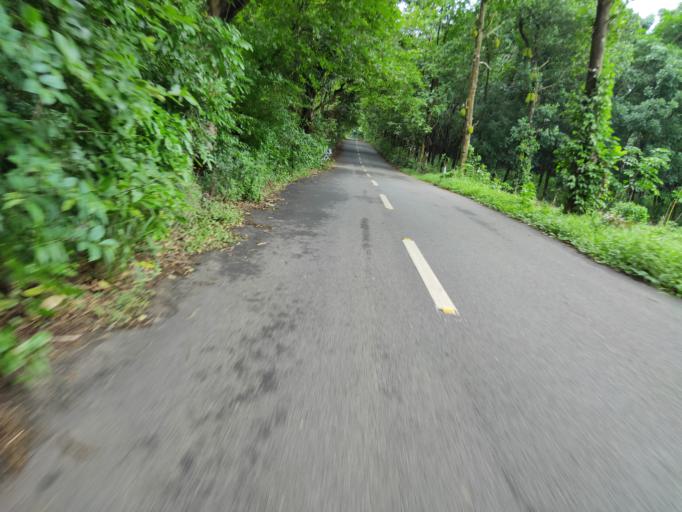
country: IN
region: Kerala
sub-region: Malappuram
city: Manjeri
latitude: 11.2236
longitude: 76.2507
